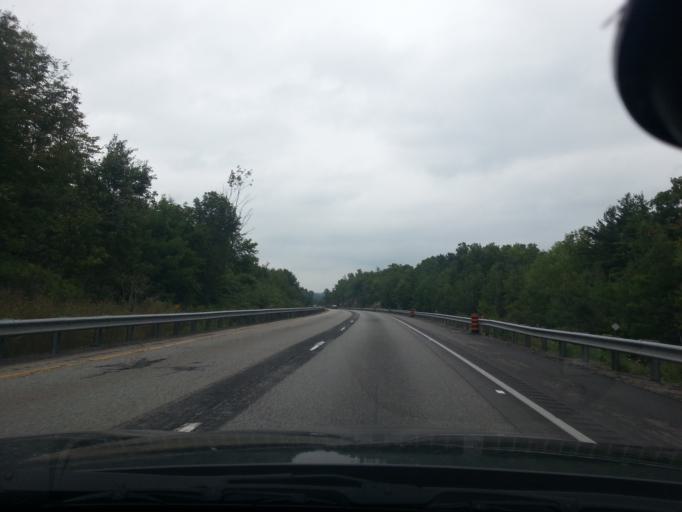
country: US
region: New York
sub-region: Jefferson County
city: Alexandria Bay
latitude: 44.4126
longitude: -75.9213
